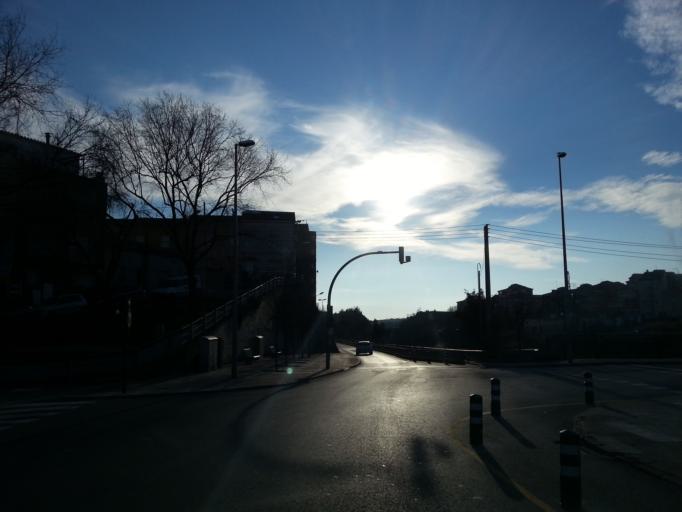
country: ES
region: Catalonia
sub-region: Provincia de Barcelona
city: Terrassa
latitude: 41.5705
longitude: 1.9997
